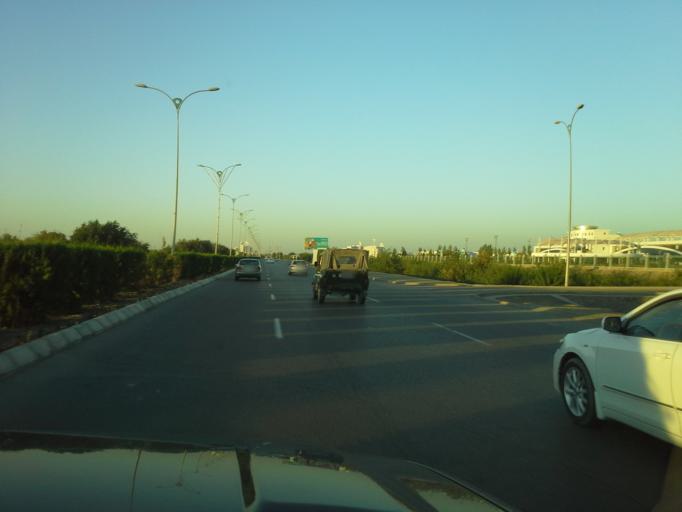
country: TM
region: Dasoguz
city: Dasoguz
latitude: 41.8129
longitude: 59.9141
